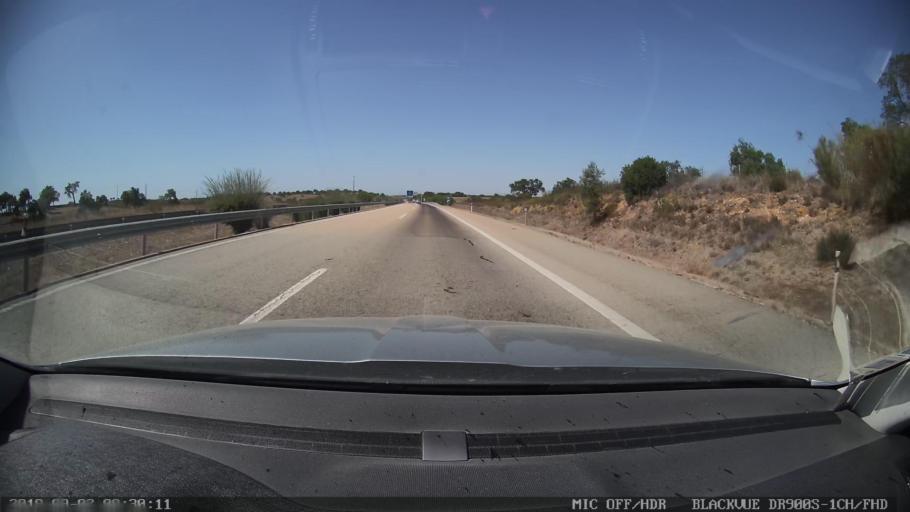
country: PT
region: Evora
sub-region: Vendas Novas
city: Vendas Novas
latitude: 38.6469
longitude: -8.4237
